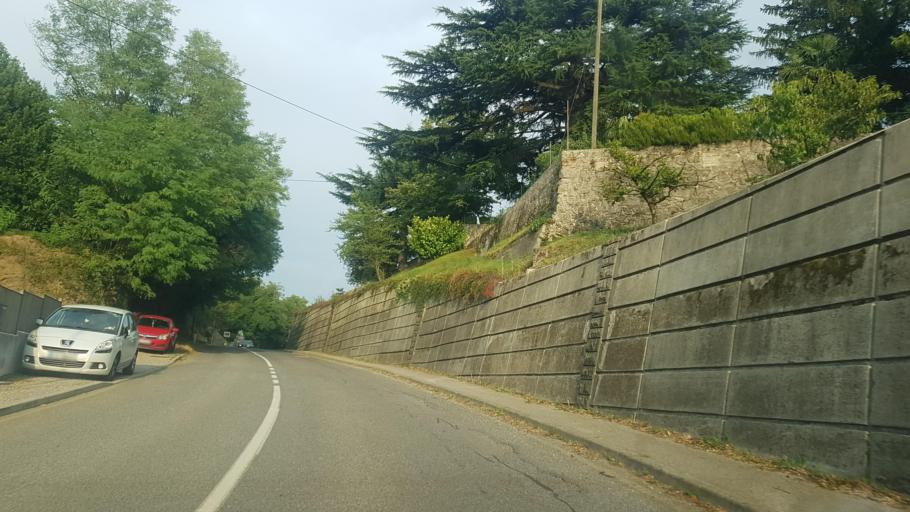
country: SI
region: Nova Gorica
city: Prvacina
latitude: 45.8875
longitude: 13.7493
